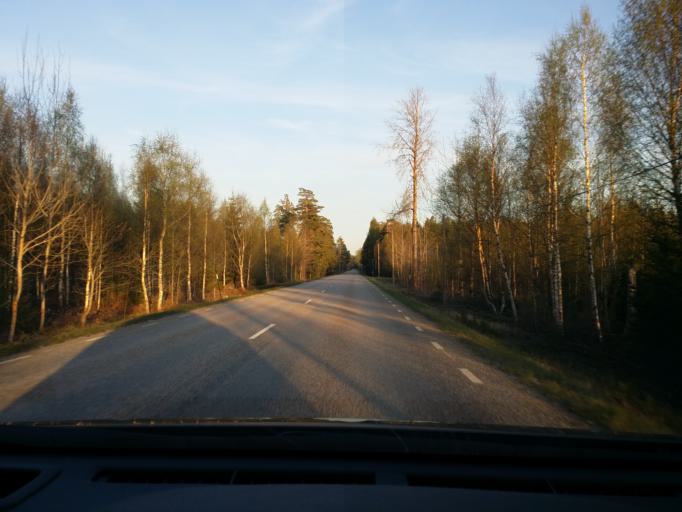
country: SE
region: Vaestmanland
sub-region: Sala Kommun
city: Sala
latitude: 59.8317
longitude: 16.5102
